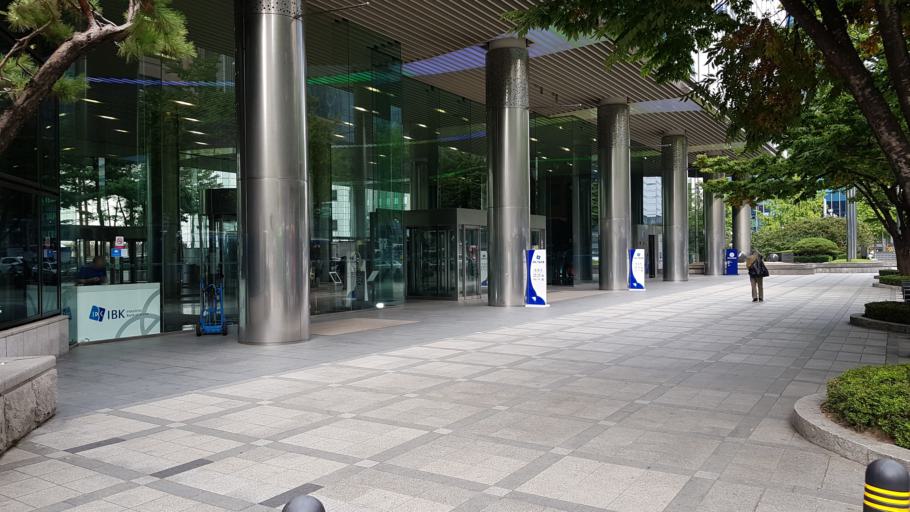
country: KR
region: Seoul
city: Seoul
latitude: 37.5660
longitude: 126.9858
